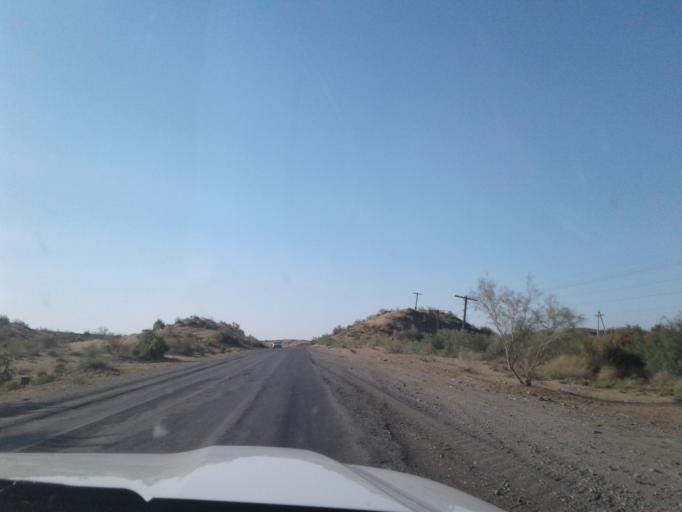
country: TM
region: Mary
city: Yoloeten
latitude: 36.9633
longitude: 62.4541
